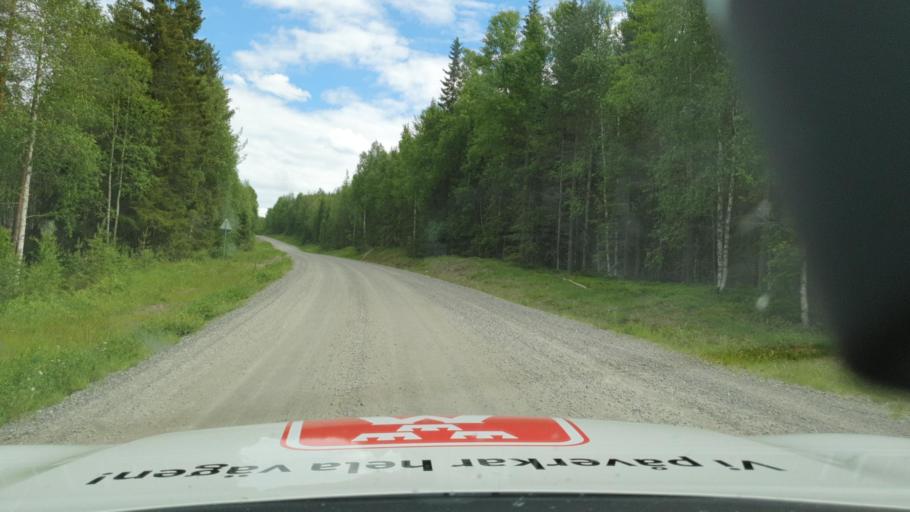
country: SE
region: Vaesterbotten
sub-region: Norsjo Kommun
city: Norsjoe
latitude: 64.8318
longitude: 19.5411
